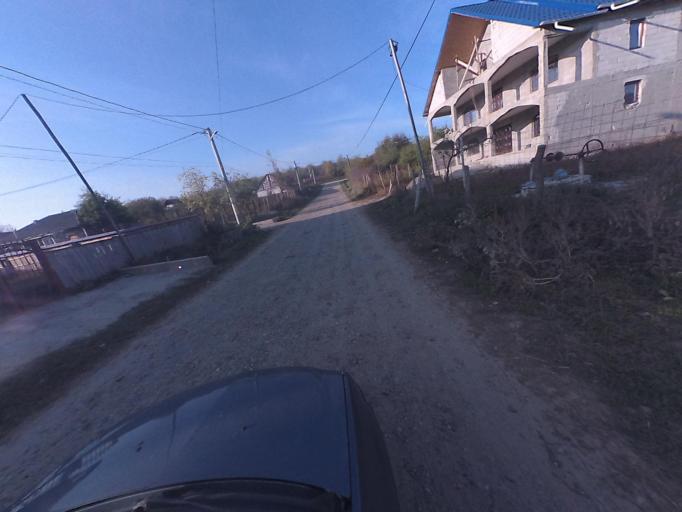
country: RO
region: Vaslui
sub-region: Comuna Bacesti
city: Bacesti
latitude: 46.8189
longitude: 27.2388
